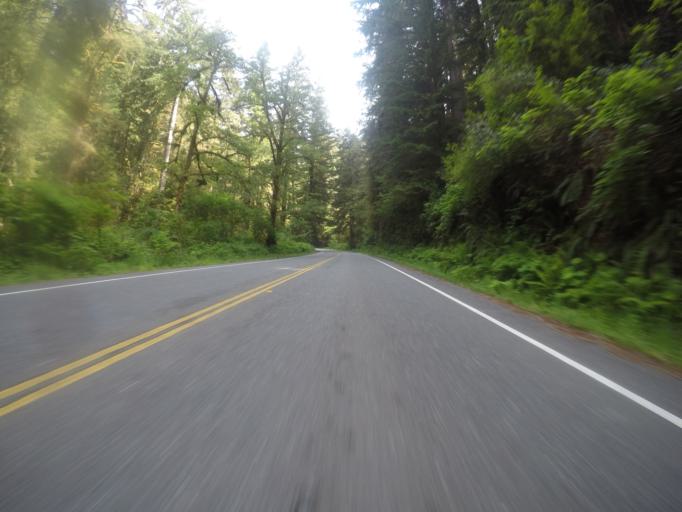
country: US
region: California
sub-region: Del Norte County
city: Bertsch-Oceanview
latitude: 41.4327
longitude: -124.0385
